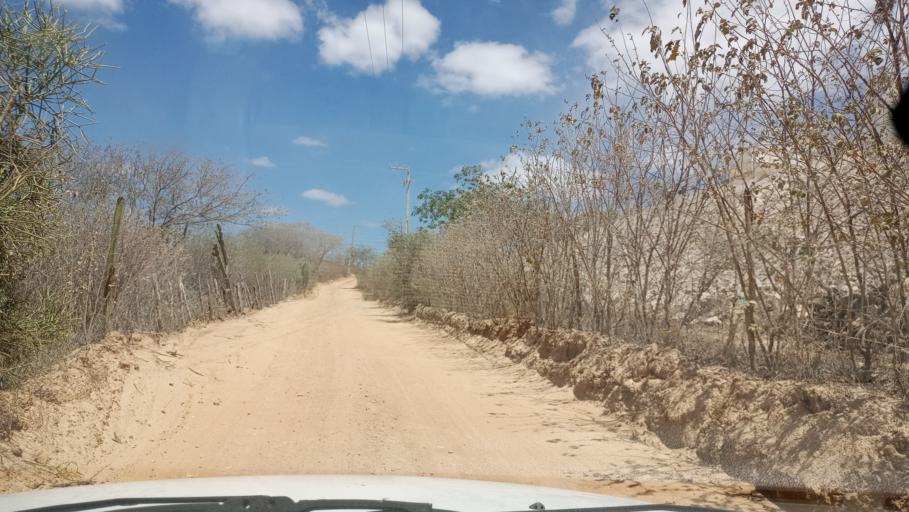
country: BR
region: Rio Grande do Norte
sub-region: Sao Paulo Do Potengi
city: Sao Paulo do Potengi
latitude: -5.7915
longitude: -35.9191
